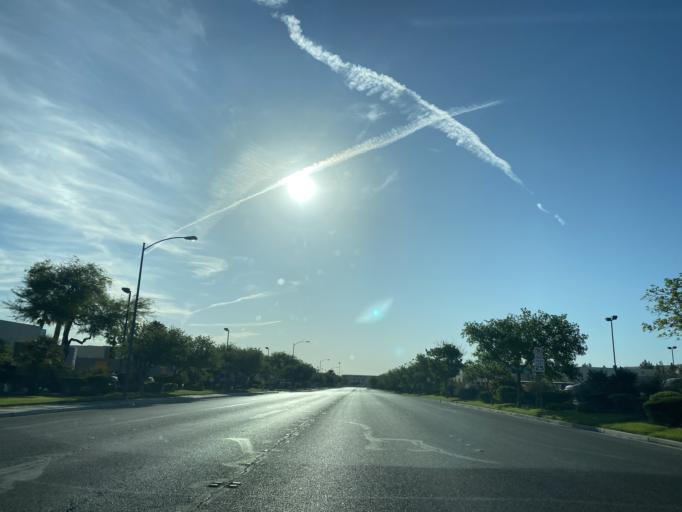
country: US
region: Nevada
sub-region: Clark County
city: Paradise
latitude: 36.0678
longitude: -115.1537
